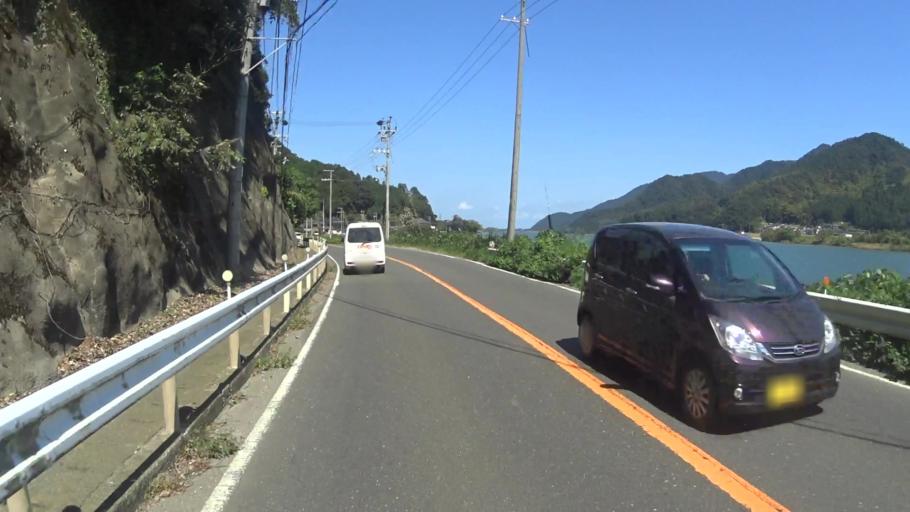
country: JP
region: Kyoto
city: Maizuru
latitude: 35.4739
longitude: 135.2771
